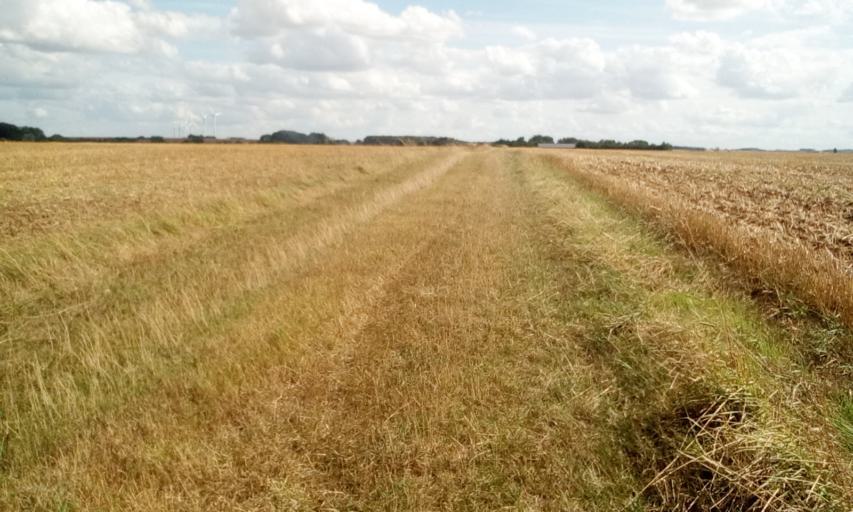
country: FR
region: Lower Normandy
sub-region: Departement du Calvados
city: Saint-Sylvain
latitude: 49.0778
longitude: -0.1978
